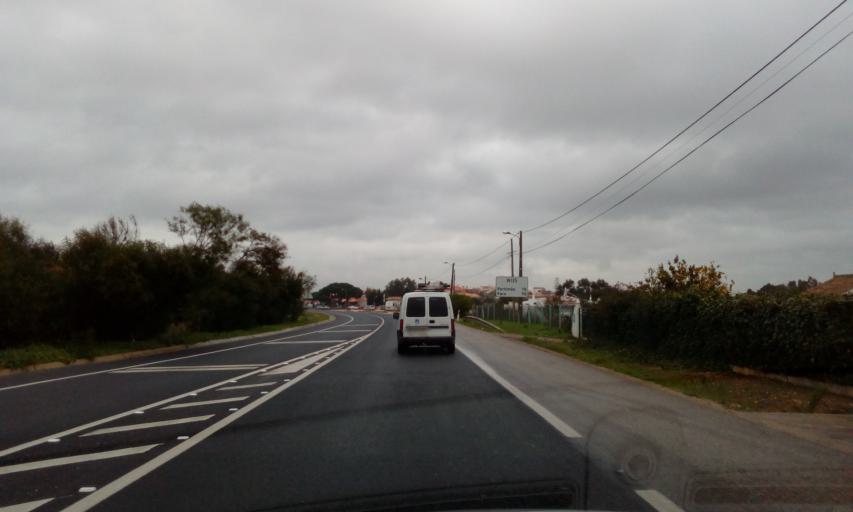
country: PT
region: Faro
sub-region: Lagos
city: Lagos
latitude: 37.1331
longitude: -8.6653
